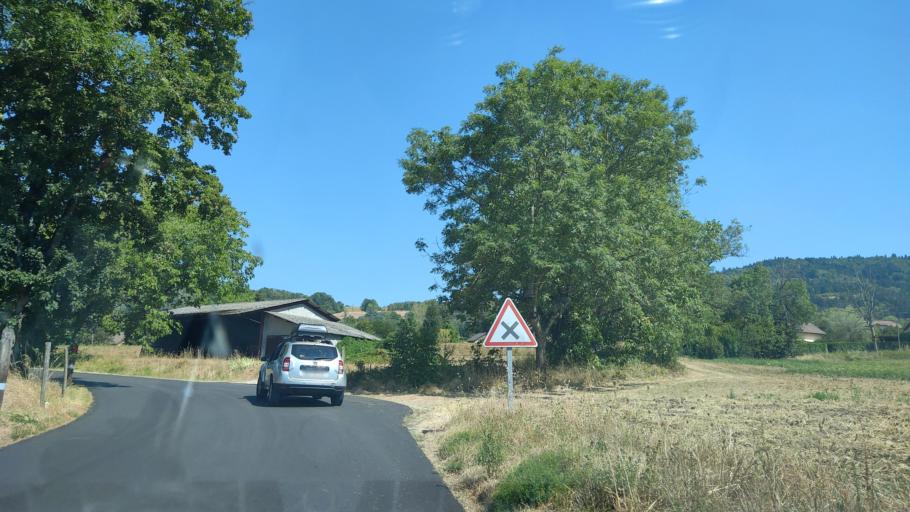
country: FR
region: Rhone-Alpes
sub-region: Departement de la Savoie
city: Novalaise
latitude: 45.5972
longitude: 5.7787
